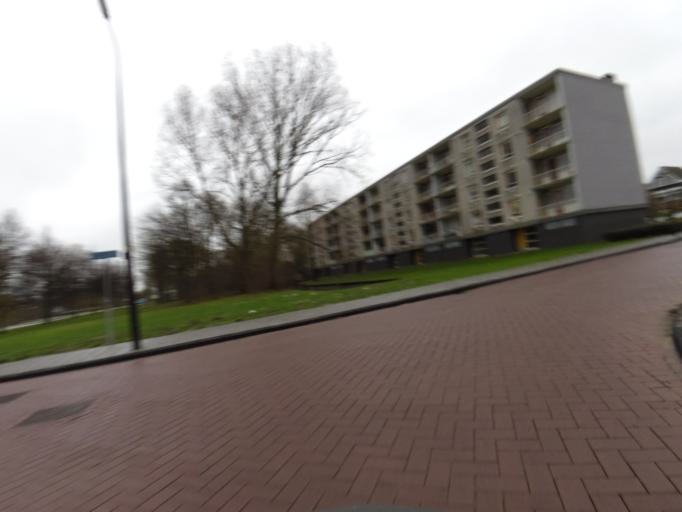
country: NL
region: South Holland
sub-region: Gemeente Maassluis
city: Maassluis
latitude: 51.9195
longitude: 4.2672
